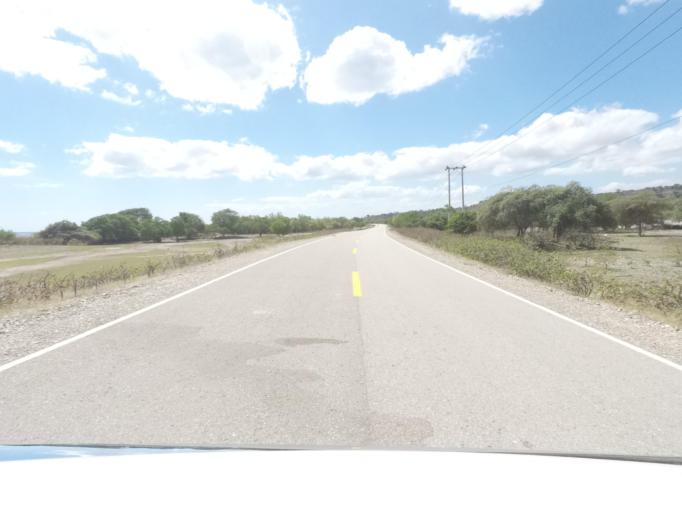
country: TL
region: Baucau
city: Baucau
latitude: -8.4424
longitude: 126.6522
